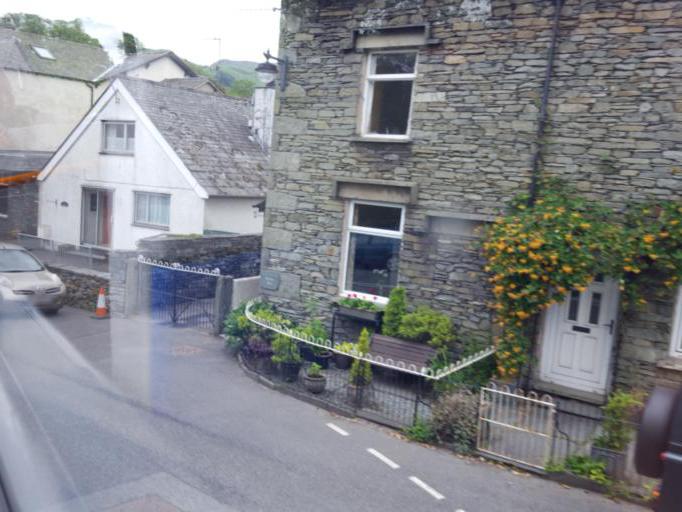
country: GB
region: England
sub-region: Cumbria
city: Ambleside
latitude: 54.4644
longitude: -3.0220
